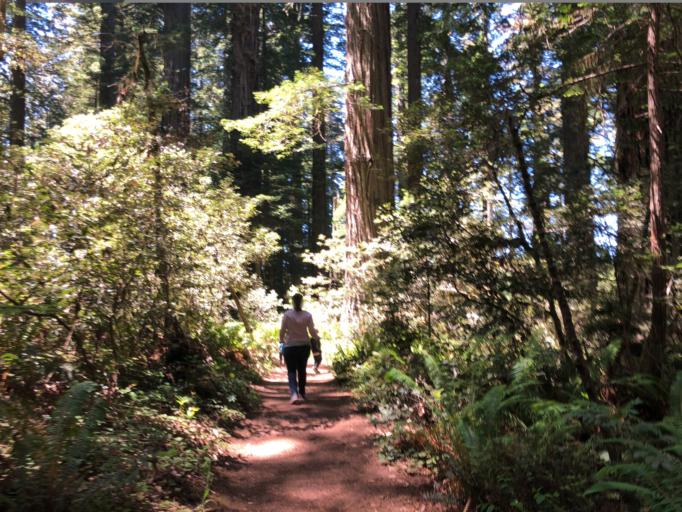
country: US
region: California
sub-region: Humboldt County
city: Westhaven-Moonstone
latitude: 41.3092
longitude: -124.0231
